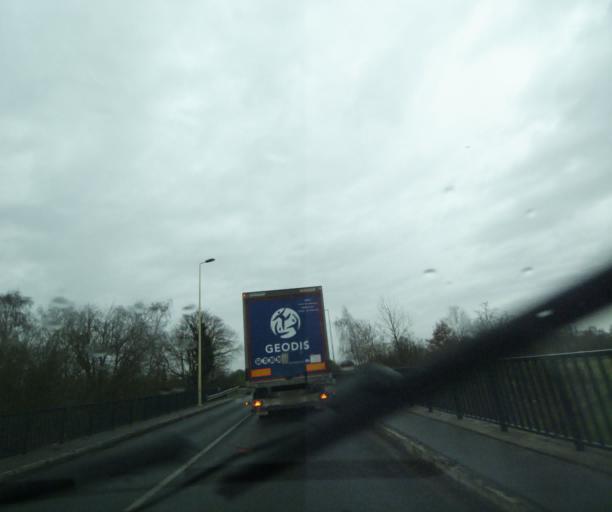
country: FR
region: Nord-Pas-de-Calais
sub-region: Departement du Nord
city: Vieux-Conde
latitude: 50.4531
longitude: 3.5647
